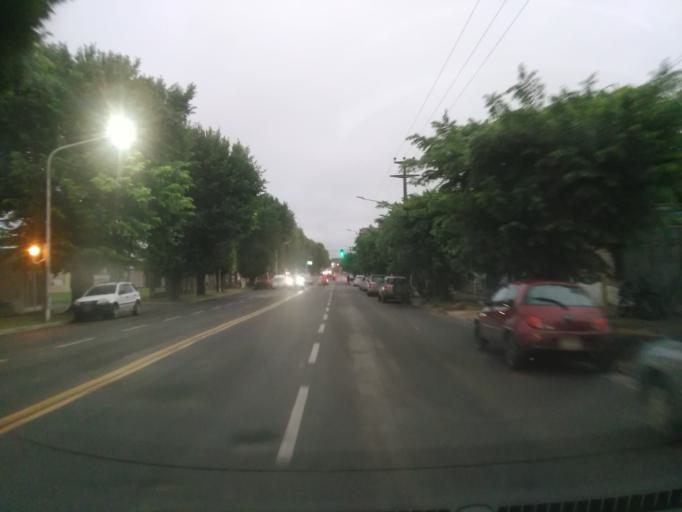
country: AR
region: Buenos Aires
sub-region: Partido de Tandil
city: Tandil
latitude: -37.3291
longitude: -59.1452
